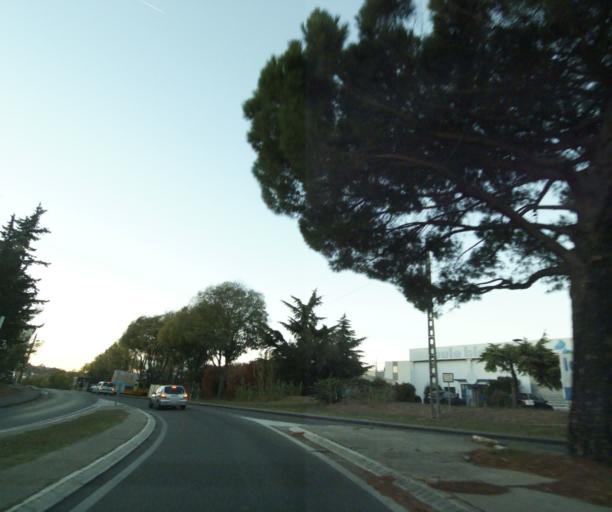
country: FR
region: Provence-Alpes-Cote d'Azur
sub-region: Departement des Bouches-du-Rhone
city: La Penne-sur-Huveaune
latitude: 43.2932
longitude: 5.4947
